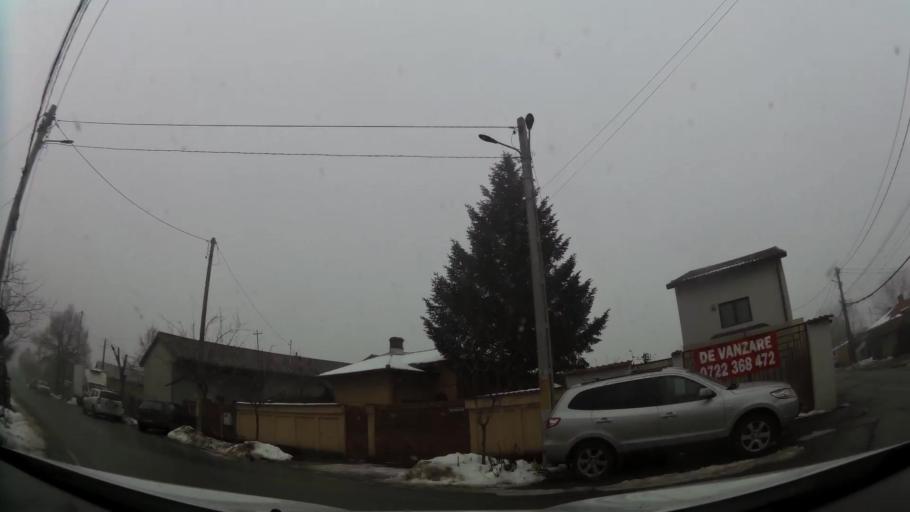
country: RO
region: Ilfov
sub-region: Comuna Chiajna
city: Chiajna
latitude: 44.4582
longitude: 25.9811
